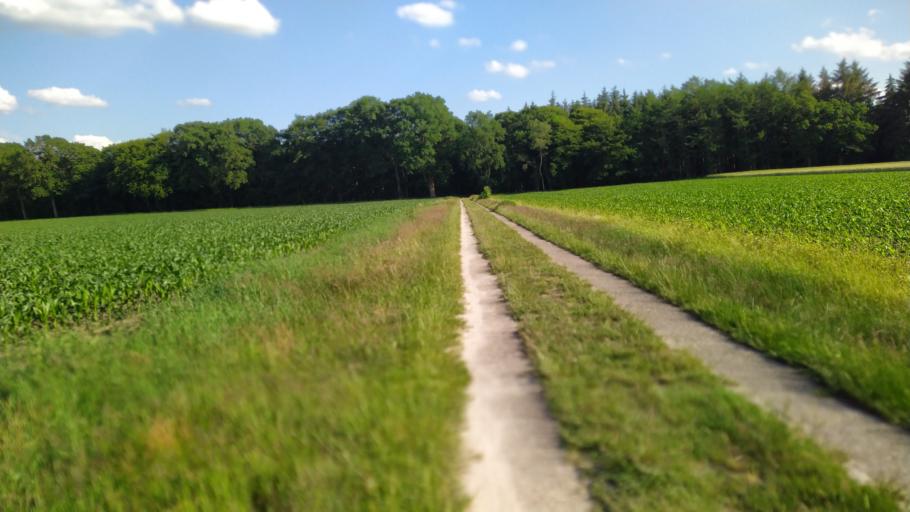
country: DE
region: Lower Saxony
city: Lintig
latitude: 53.5991
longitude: 8.8938
